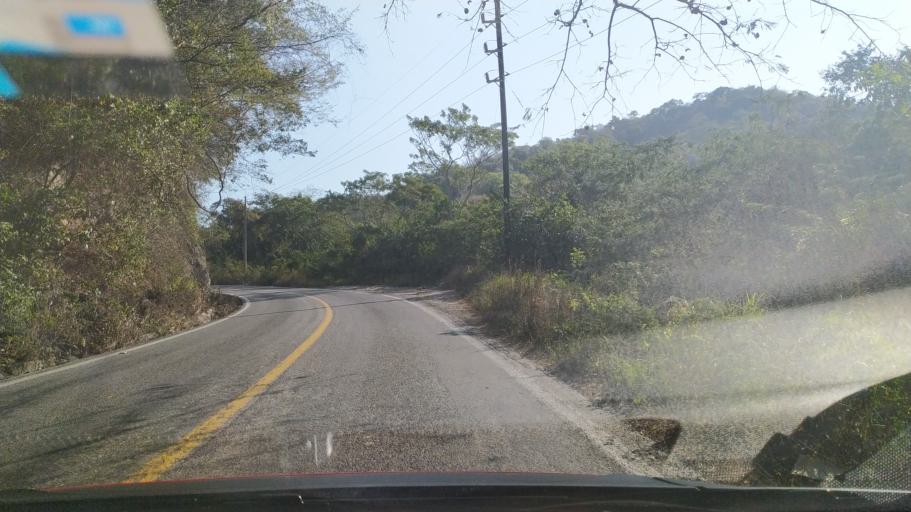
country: MX
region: Michoacan
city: Coahuayana Viejo
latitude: 18.6140
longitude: -103.6783
